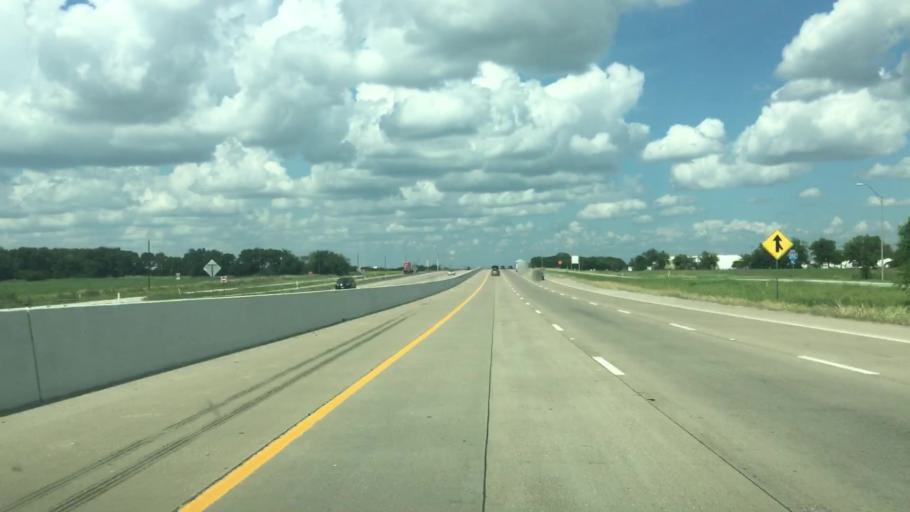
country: US
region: Texas
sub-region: Ellis County
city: Italy
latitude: 32.1988
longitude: -96.8977
